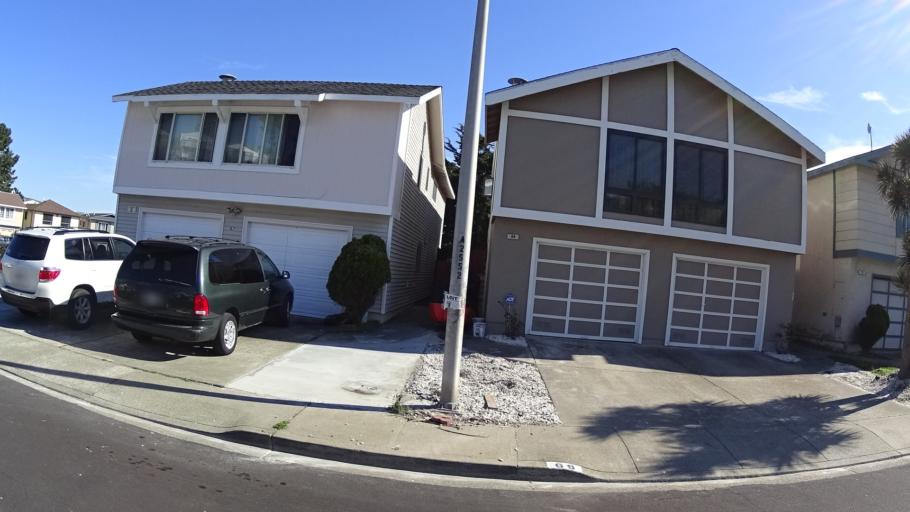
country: US
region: California
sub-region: San Mateo County
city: Colma
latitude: 37.6512
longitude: -122.4596
